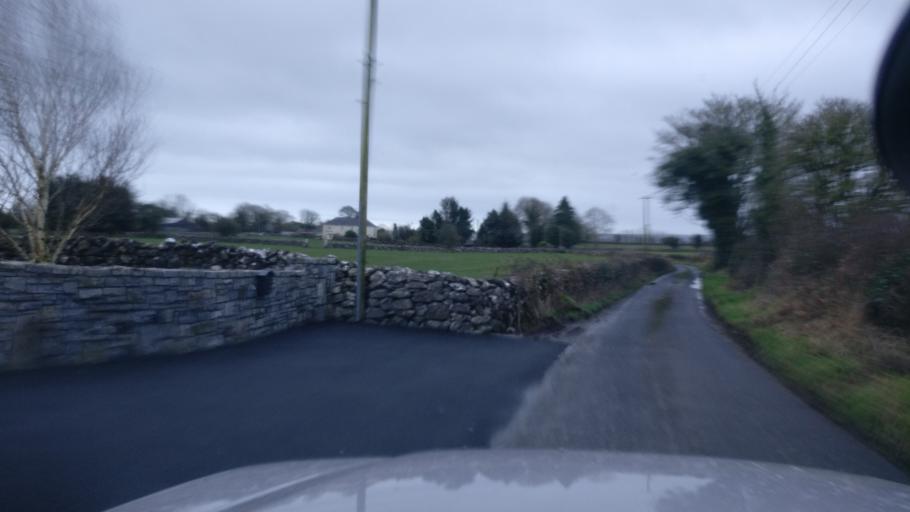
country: IE
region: Connaught
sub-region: County Galway
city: Loughrea
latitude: 53.2014
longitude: -8.6443
